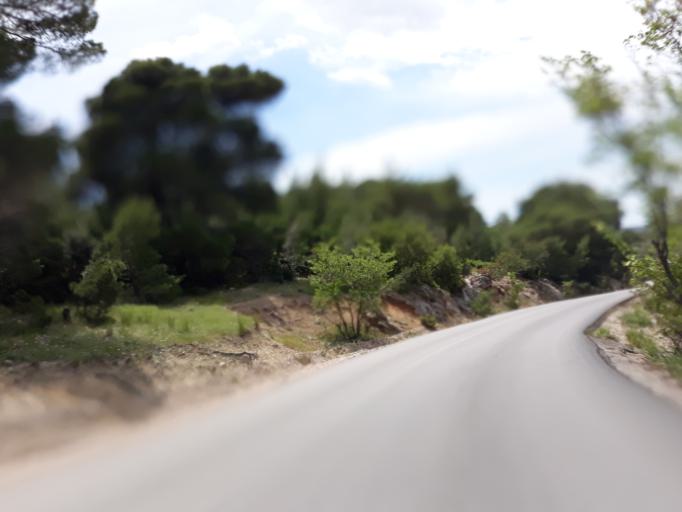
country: GR
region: Attica
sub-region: Nomarchia Dytikis Attikis
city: Magoula
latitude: 38.1507
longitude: 23.5185
